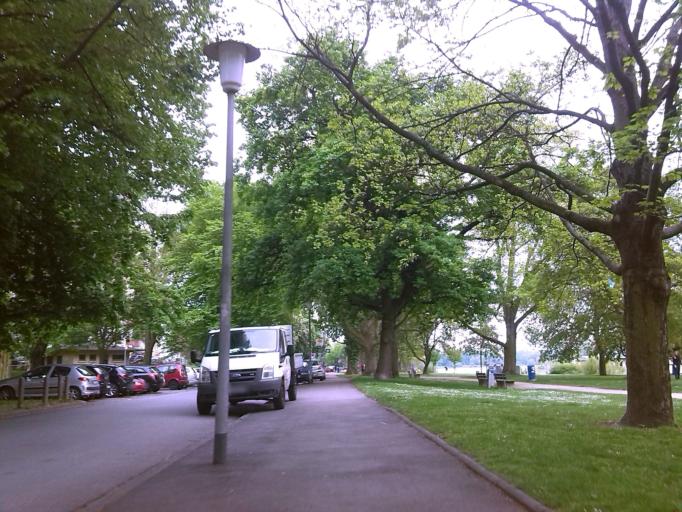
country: DE
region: Rheinland-Pfalz
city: Ludwigshafen am Rhein
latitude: 49.4761
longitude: 8.4636
